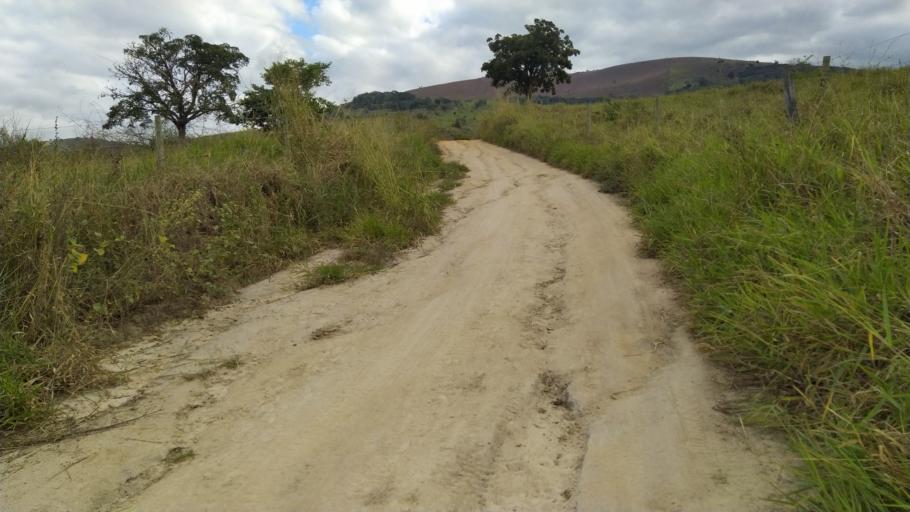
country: BR
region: Minas Gerais
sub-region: Almenara
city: Almenara
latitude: -16.6295
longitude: -40.4589
